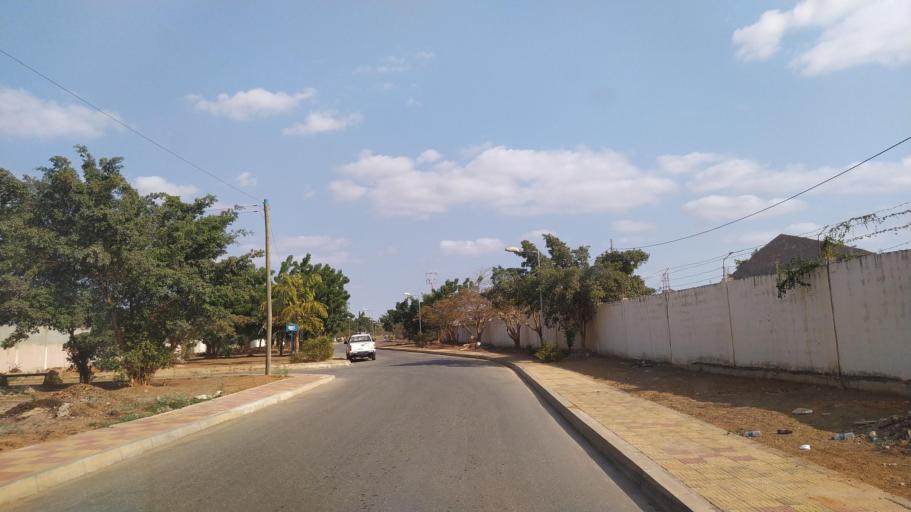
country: AO
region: Luanda
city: Luanda
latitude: -8.8928
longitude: 13.2572
